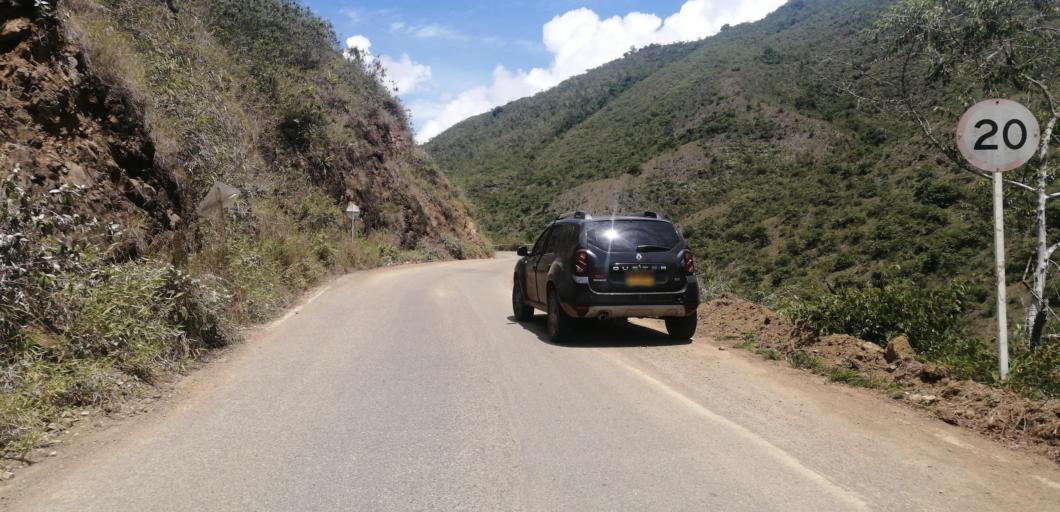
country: CO
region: Valle del Cauca
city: Restrepo
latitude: 3.7195
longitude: -76.5831
